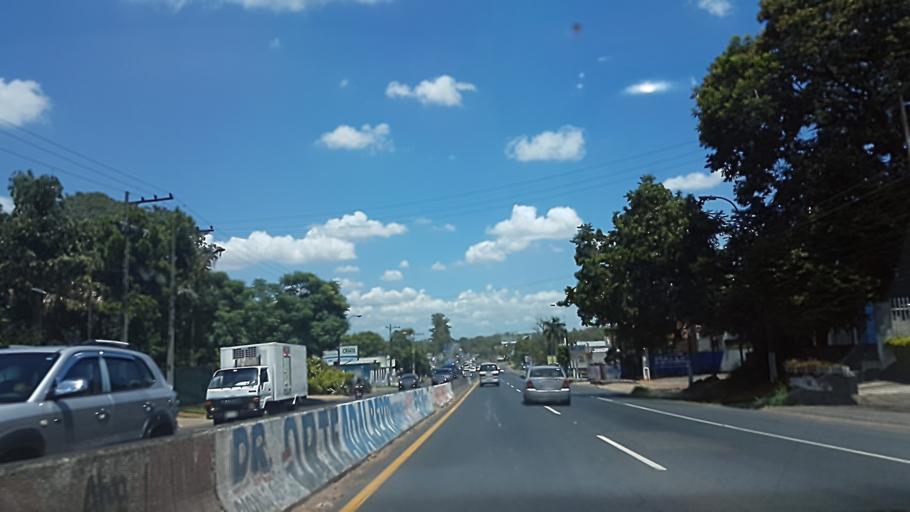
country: PY
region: Central
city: Capiata
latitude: -25.3462
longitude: -57.4762
